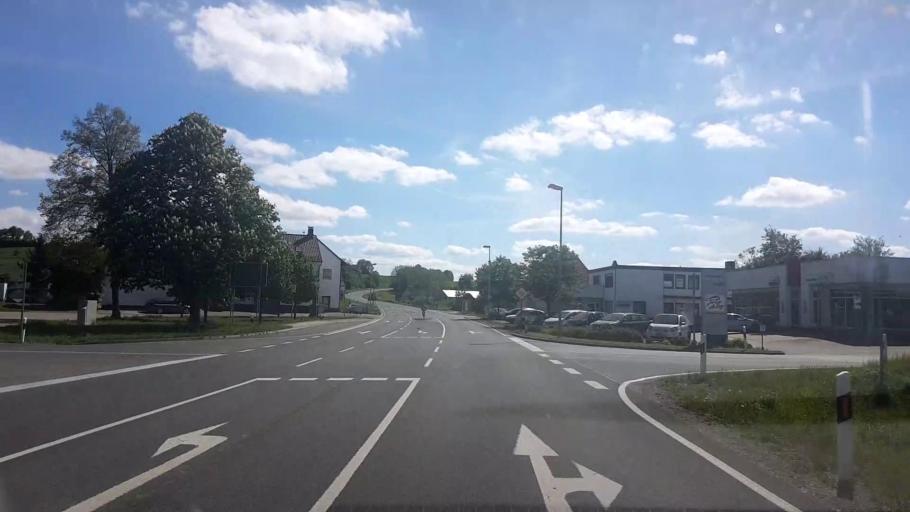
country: DE
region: Bavaria
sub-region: Regierungsbezirk Unterfranken
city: Untermerzbach
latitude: 50.0806
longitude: 10.8671
